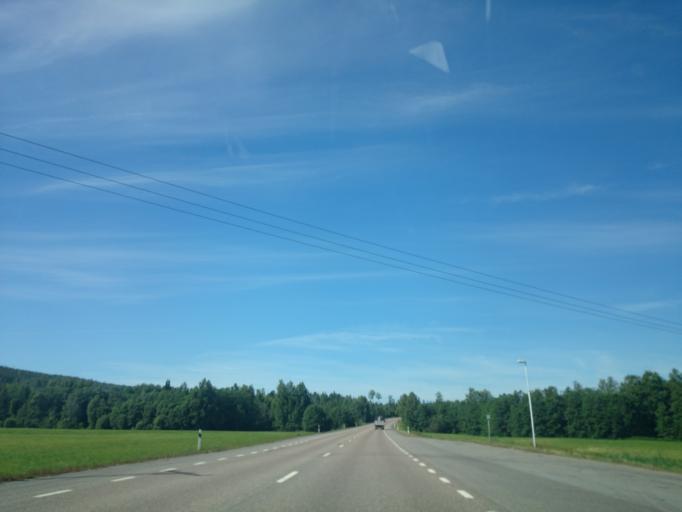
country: SE
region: Vaesternorrland
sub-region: Sundsvalls Kommun
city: Vi
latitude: 62.3812
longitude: 17.1593
